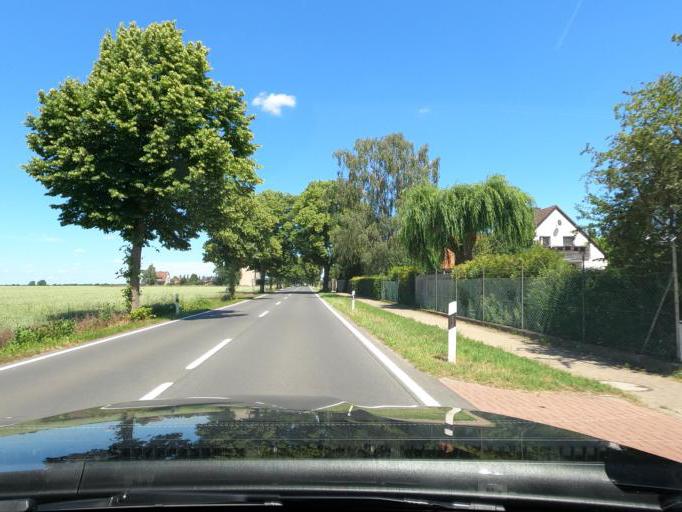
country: DE
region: Lower Saxony
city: Lehrte
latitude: 52.4068
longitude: 9.9741
